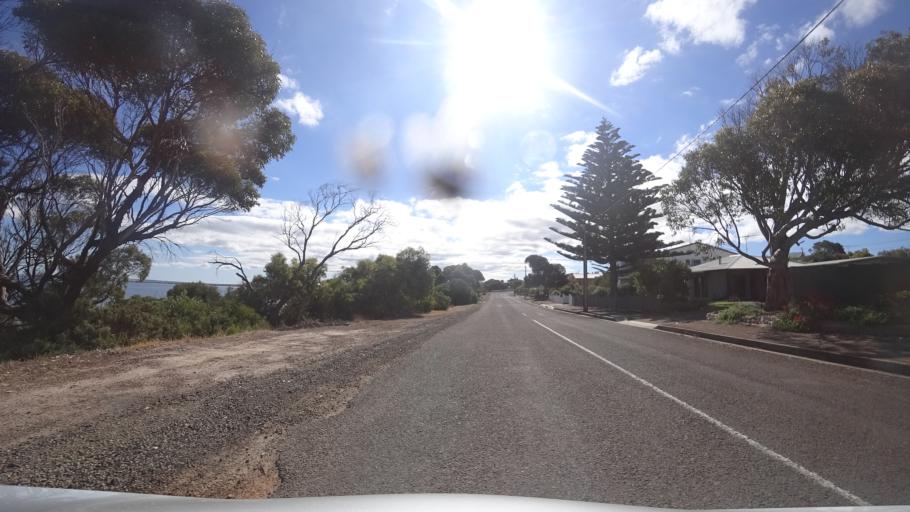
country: AU
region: South Australia
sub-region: Kangaroo Island
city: Kingscote
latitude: -35.6600
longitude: 137.6345
